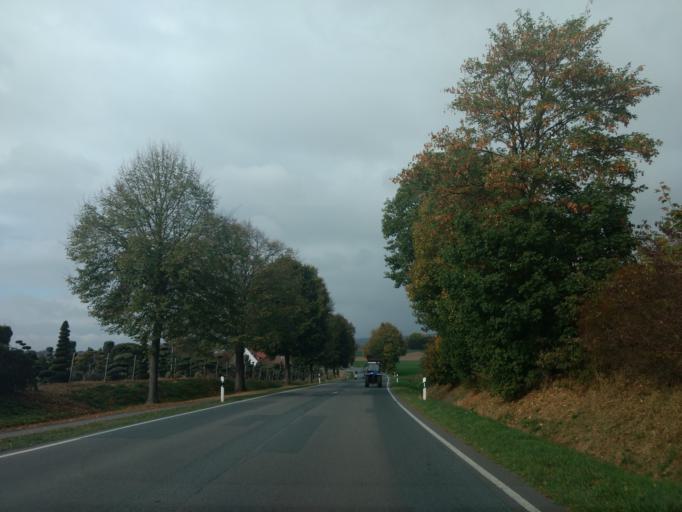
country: DE
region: Lower Saxony
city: Bad Iburg
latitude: 52.1459
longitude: 8.0719
